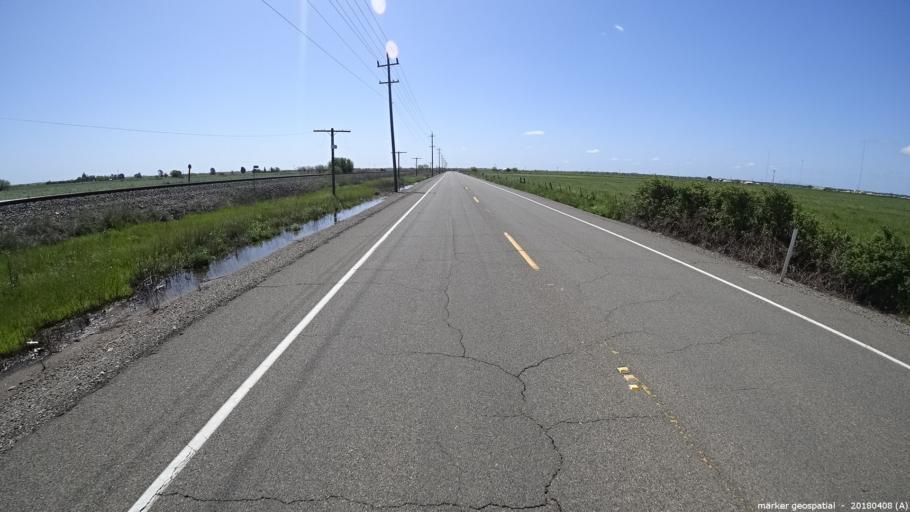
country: US
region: California
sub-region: San Joaquin County
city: Thornton
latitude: 38.2960
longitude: -121.4416
